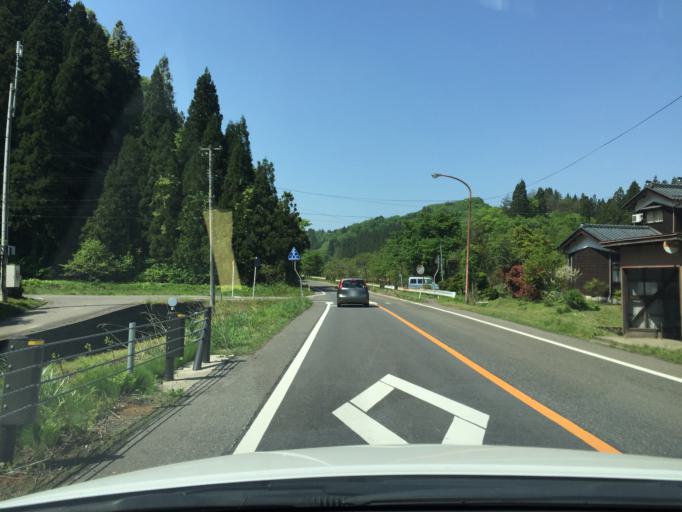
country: JP
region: Niigata
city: Muramatsu
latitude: 37.6505
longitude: 139.1330
